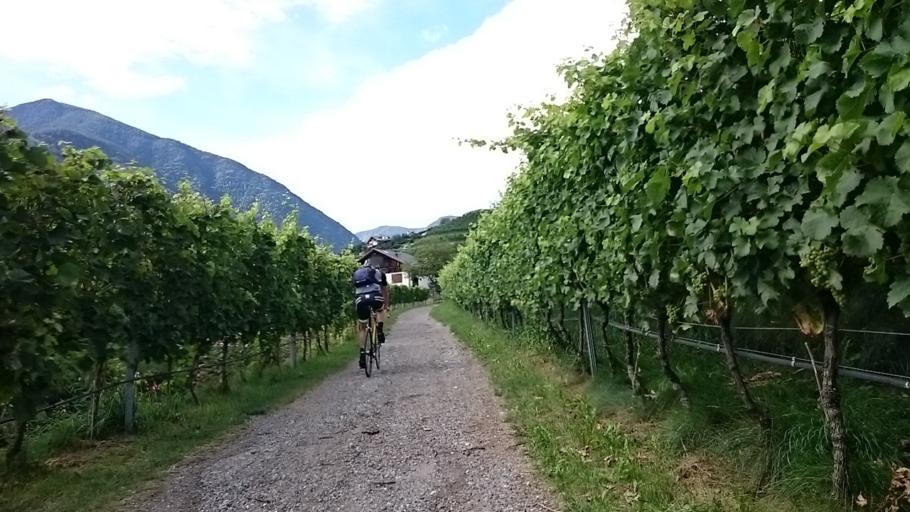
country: IT
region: Trentino-Alto Adige
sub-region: Bolzano
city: Varna
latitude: 46.7382
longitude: 11.6435
